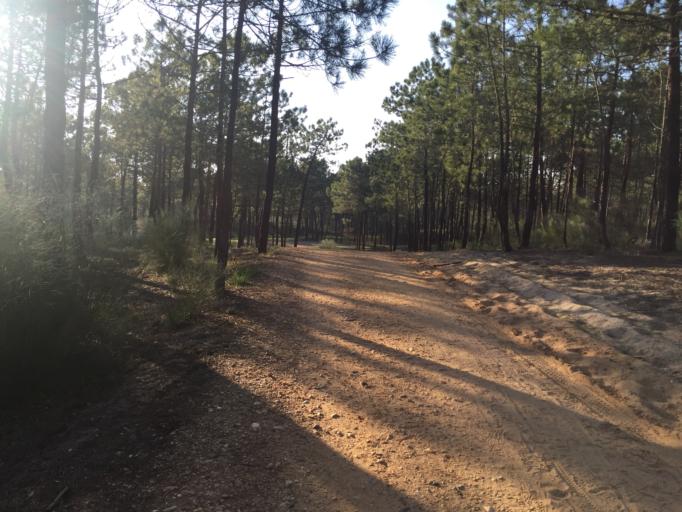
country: PT
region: Faro
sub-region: Vila Real de Santo Antonio
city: Vila Real de Santo Antonio
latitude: 37.1871
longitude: -7.4329
